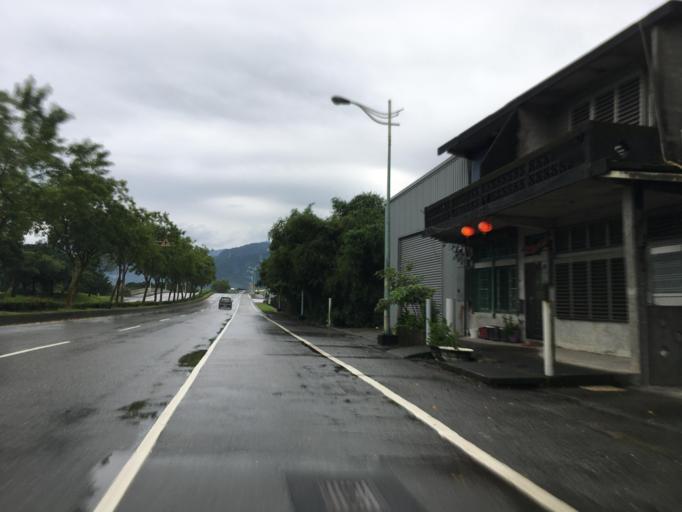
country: TW
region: Taiwan
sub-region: Yilan
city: Yilan
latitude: 24.6410
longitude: 121.7867
